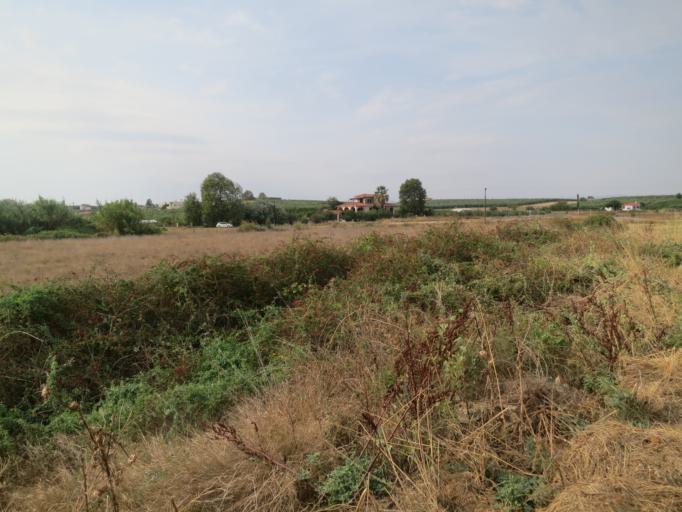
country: GR
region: Central Macedonia
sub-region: Nomos Chalkidikis
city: Nea Flogita
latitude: 40.2515
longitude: 23.2447
